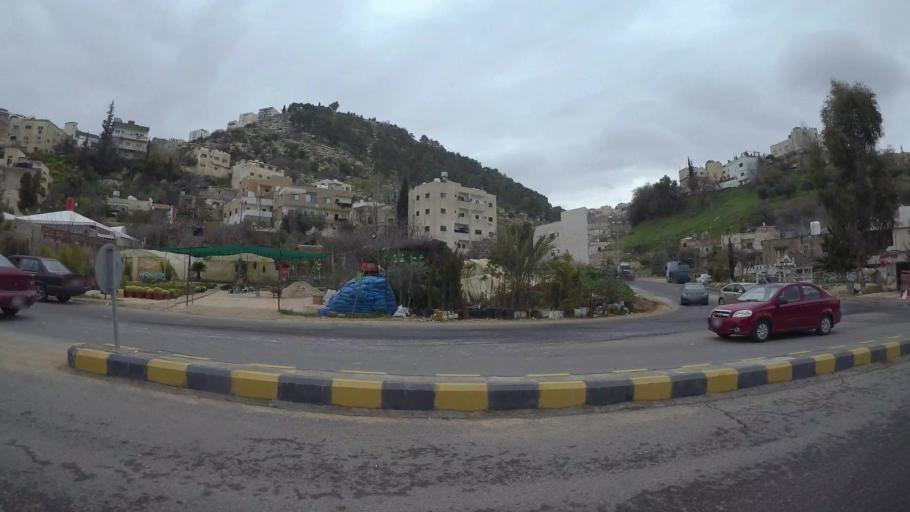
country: JO
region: Amman
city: Wadi as Sir
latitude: 31.9573
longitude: 35.8175
